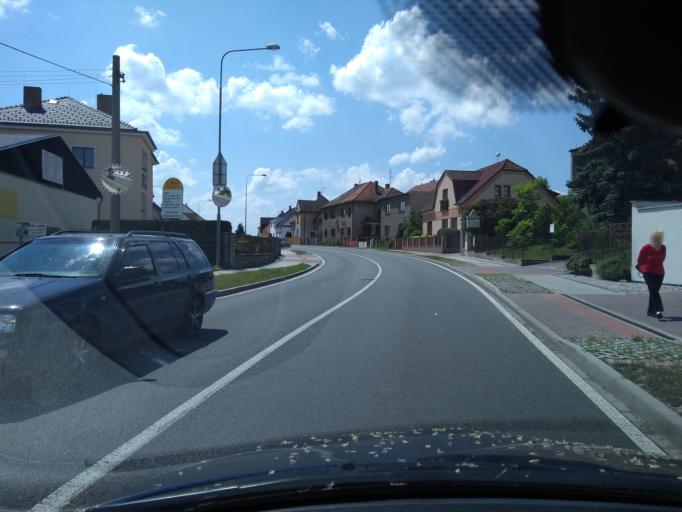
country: CZ
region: Plzensky
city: Prestice
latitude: 49.5478
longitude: 13.3160
